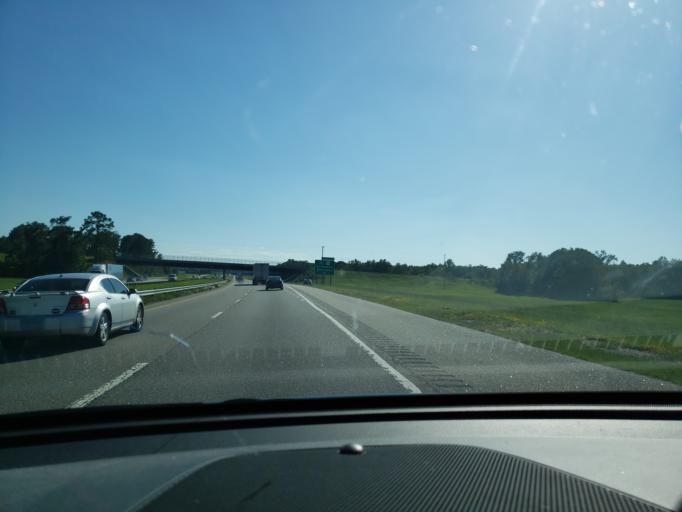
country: US
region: North Carolina
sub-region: Robeson County
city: Lumberton
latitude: 34.6030
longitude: -79.1016
